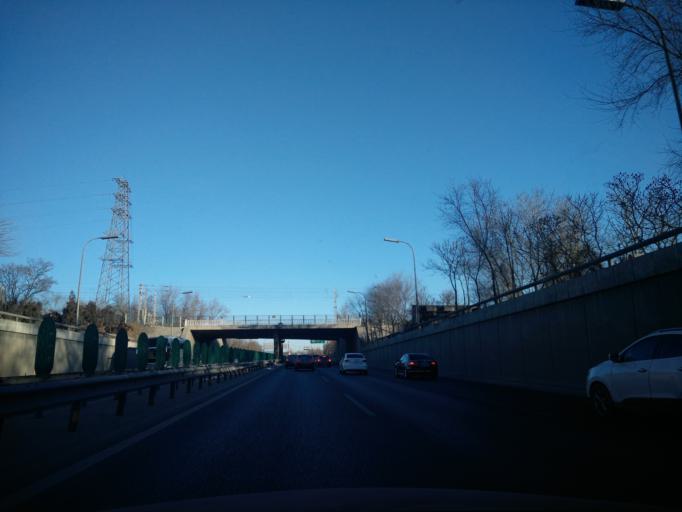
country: CN
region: Beijing
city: Lugu
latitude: 39.8514
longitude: 116.2149
